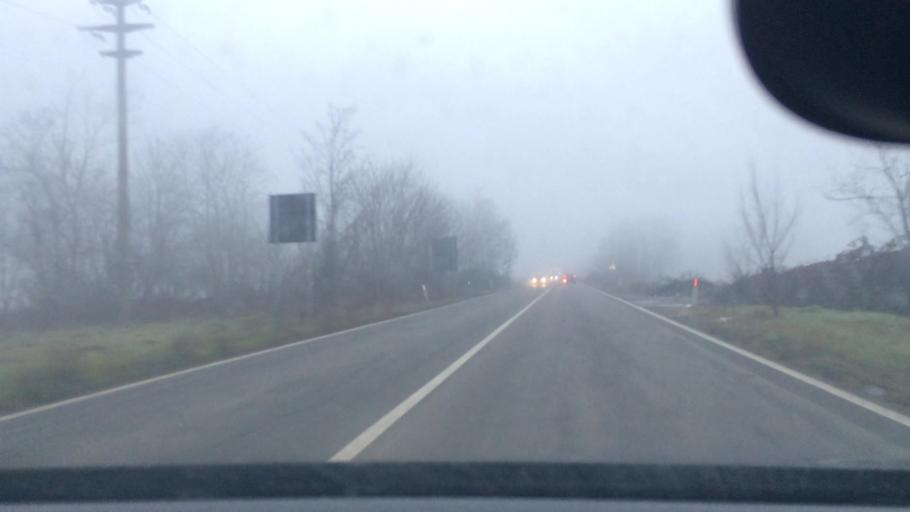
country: IT
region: Lombardy
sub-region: Citta metropolitana di Milano
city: Cantalupo
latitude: 45.5645
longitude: 8.9934
